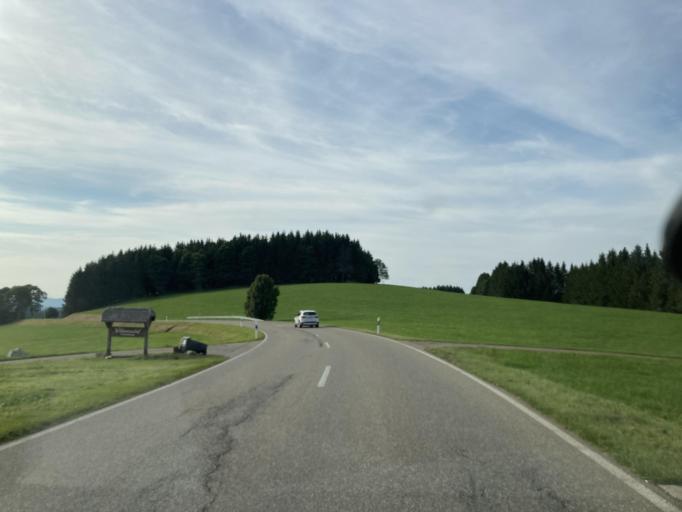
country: DE
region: Baden-Wuerttemberg
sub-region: Freiburg Region
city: Sankt Margen
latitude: 47.9841
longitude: 8.1226
